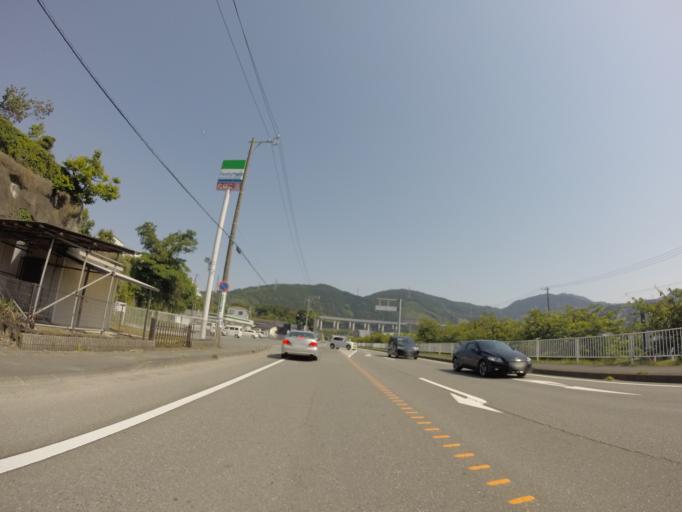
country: JP
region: Shizuoka
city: Fujinomiya
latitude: 35.1850
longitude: 138.6018
